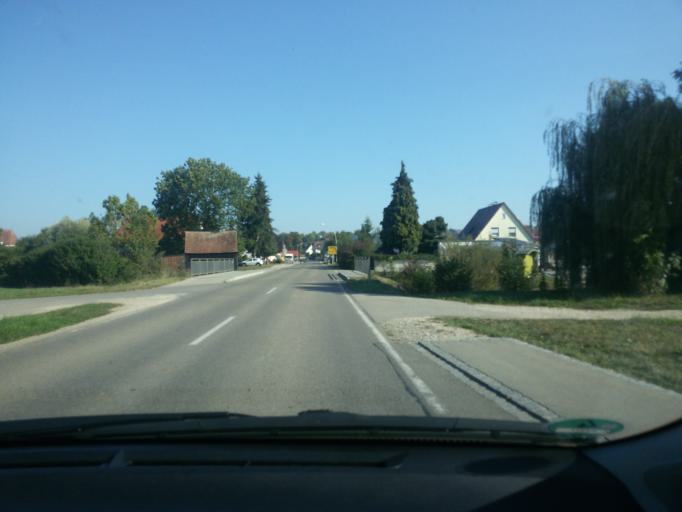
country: DE
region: Bavaria
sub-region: Swabia
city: Auhausen
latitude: 49.0043
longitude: 10.6213
